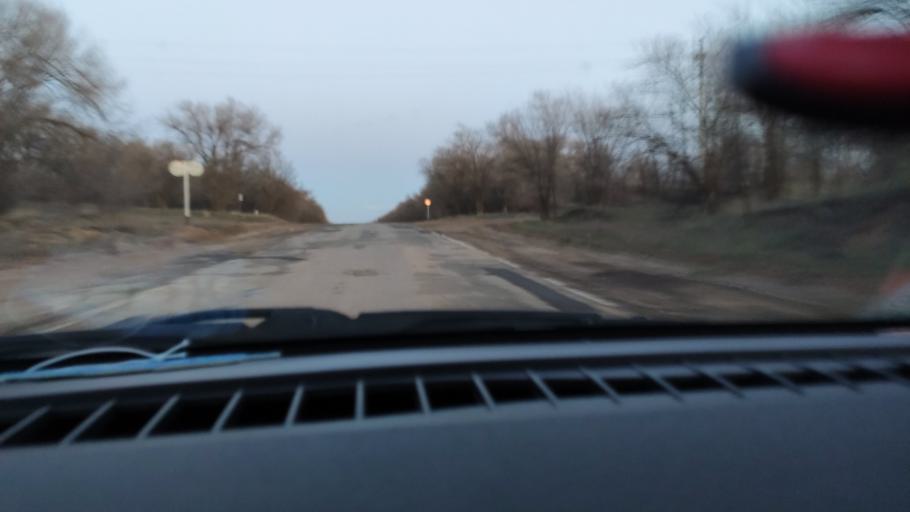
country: RU
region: Saratov
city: Krasnoarmeysk
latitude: 51.0773
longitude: 45.9734
